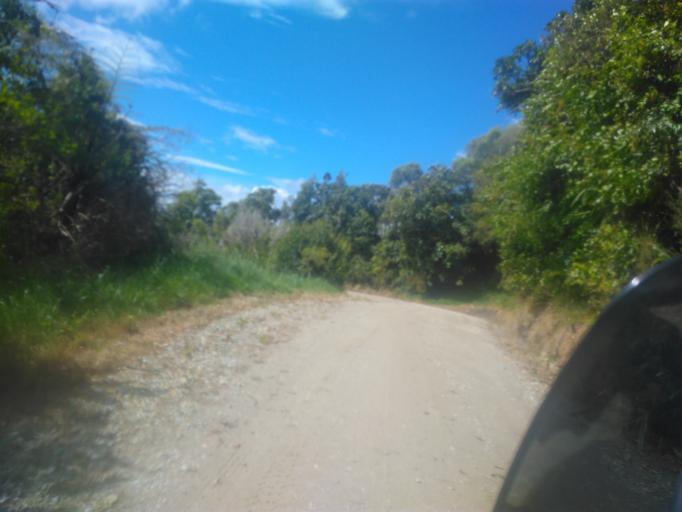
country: NZ
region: Hawke's Bay
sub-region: Wairoa District
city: Wairoa
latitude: -38.7802
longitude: 177.6221
